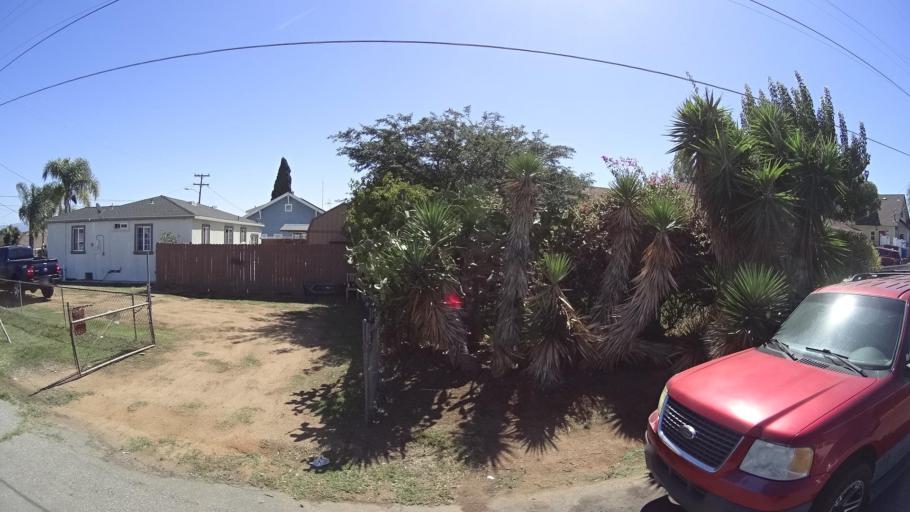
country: US
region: California
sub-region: San Diego County
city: National City
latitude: 32.6645
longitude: -117.0830
